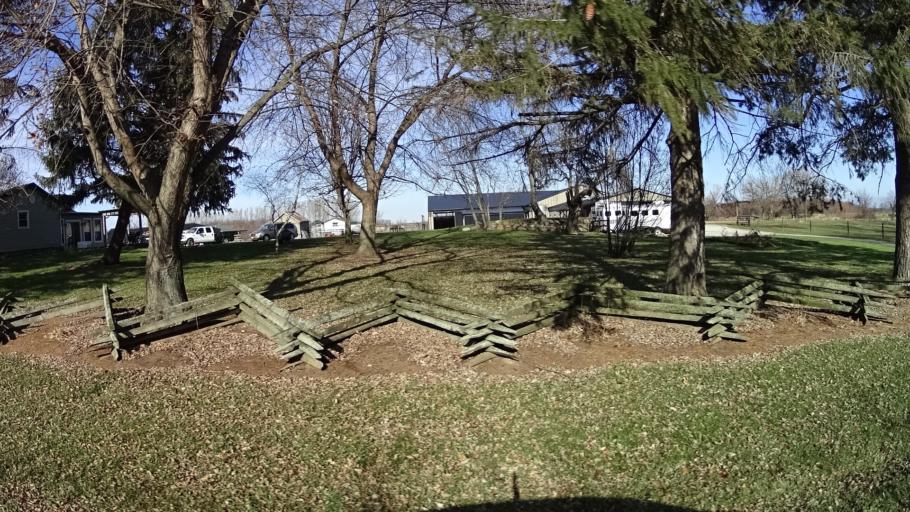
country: US
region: Ohio
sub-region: Lorain County
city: Wellington
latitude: 41.0852
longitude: -82.2383
